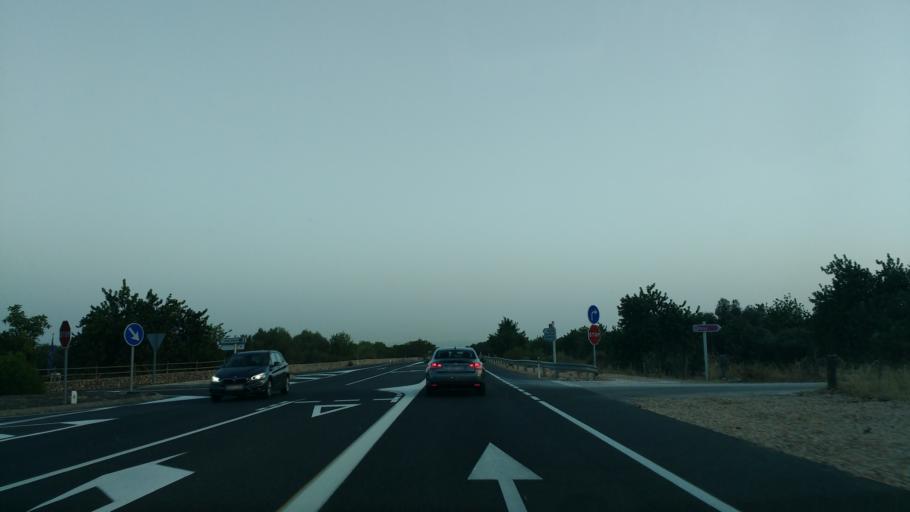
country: ES
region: Balearic Islands
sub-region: Illes Balears
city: Bunyola
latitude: 39.6753
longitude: 2.6792
